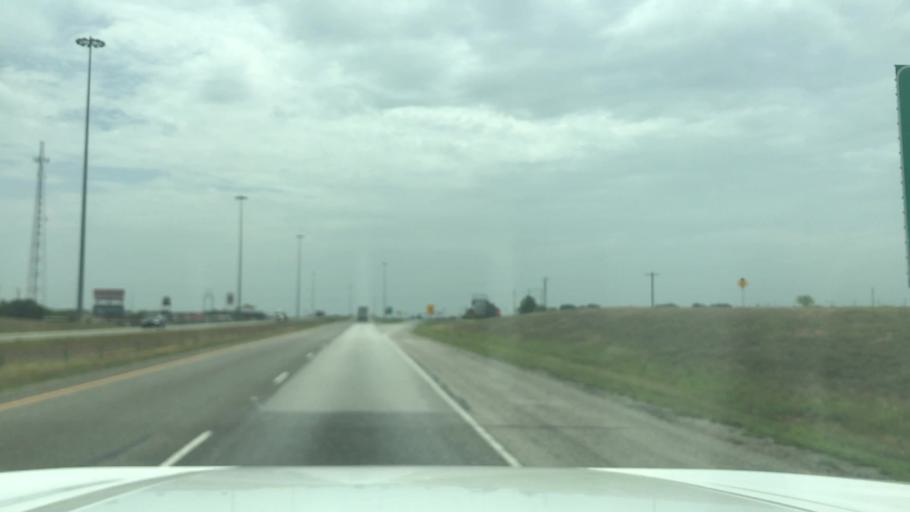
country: US
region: Texas
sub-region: Eastland County
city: Cisco
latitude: 32.3744
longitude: -98.9774
